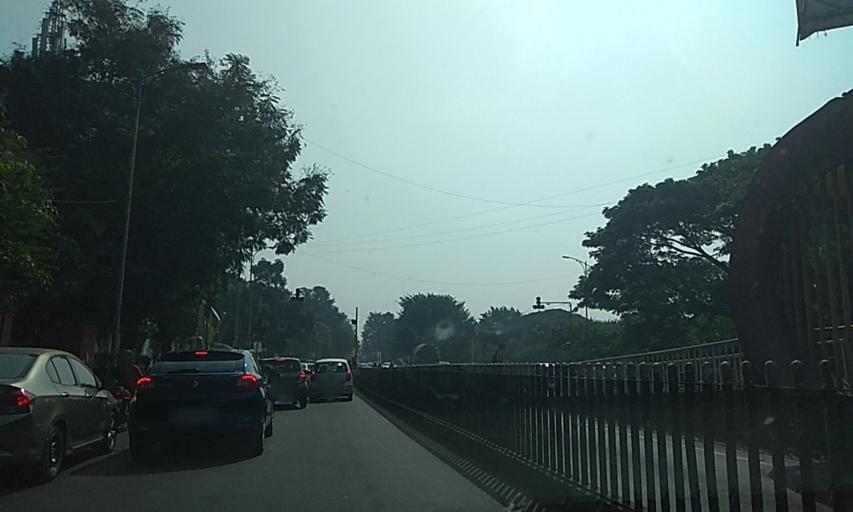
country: IN
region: Maharashtra
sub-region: Pune Division
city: Shivaji Nagar
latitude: 18.5454
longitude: 73.8764
